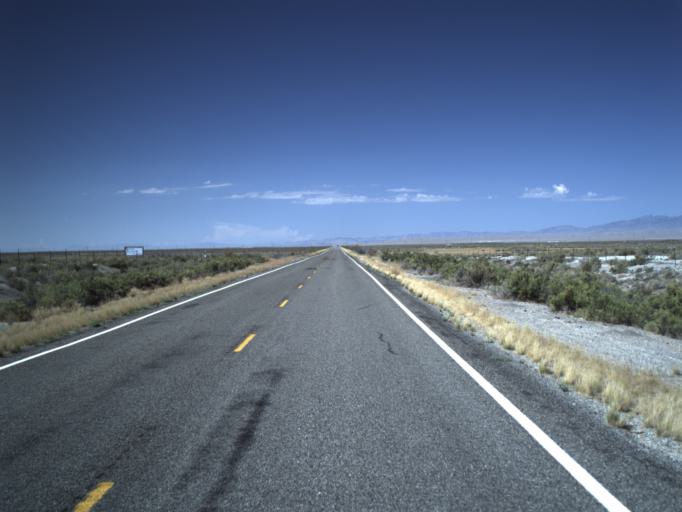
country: US
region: Utah
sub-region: Millard County
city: Delta
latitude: 39.2871
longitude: -112.8342
